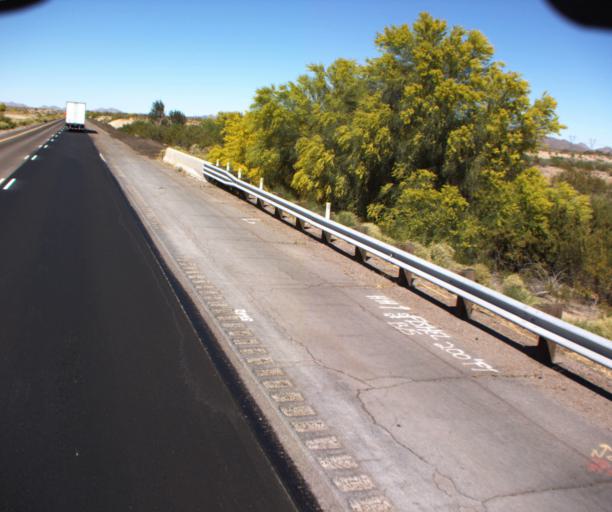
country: US
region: Arizona
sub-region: Maricopa County
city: Gila Bend
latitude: 33.0748
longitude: -112.6463
